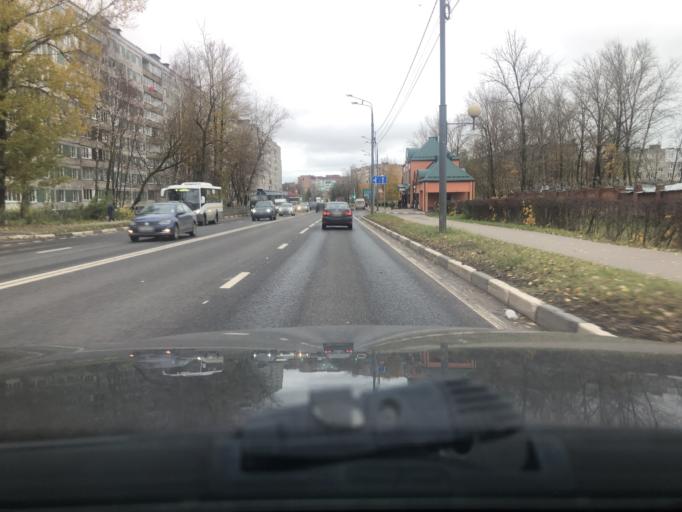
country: RU
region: Moskovskaya
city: Sergiyev Posad
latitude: 56.3309
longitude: 38.1314
